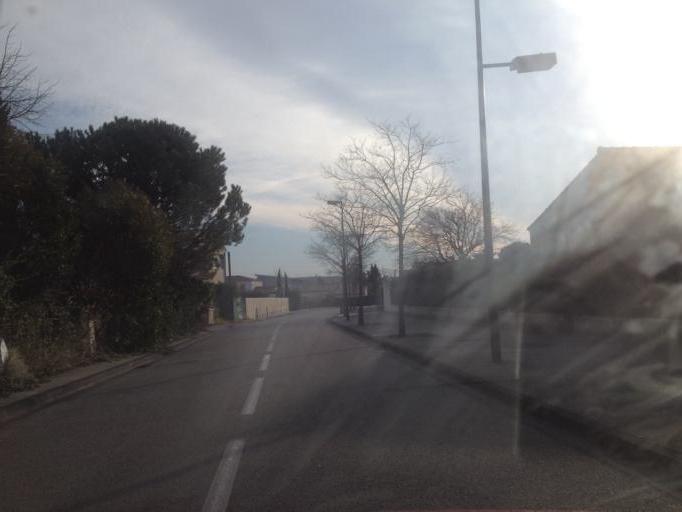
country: FR
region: Provence-Alpes-Cote d'Azur
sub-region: Departement du Vaucluse
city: Orange
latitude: 44.1449
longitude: 4.7974
